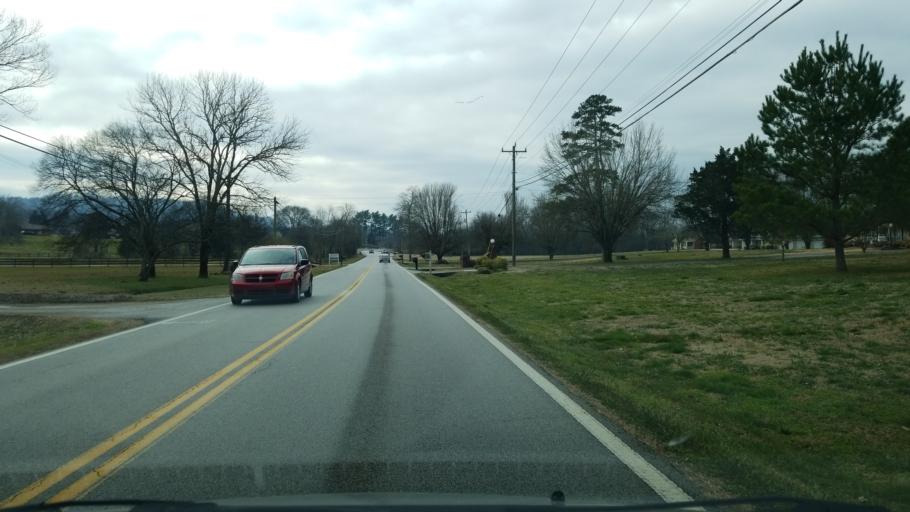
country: US
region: Tennessee
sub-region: Hamilton County
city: Collegedale
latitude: 35.0111
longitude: -85.0905
